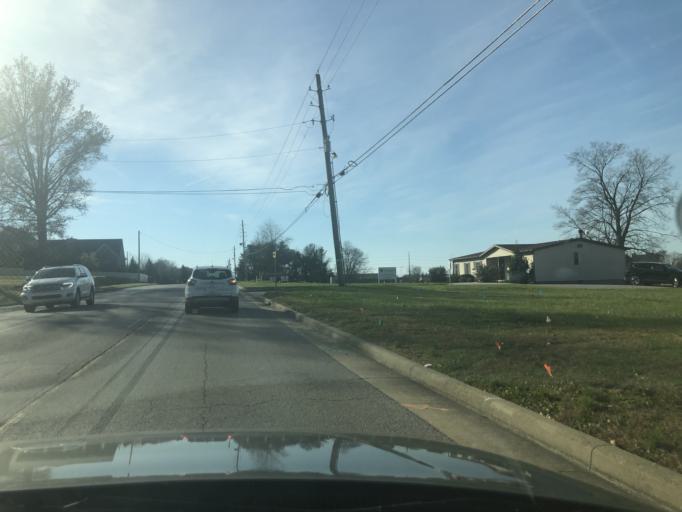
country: US
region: Indiana
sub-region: Warrick County
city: Newburgh
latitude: 37.9727
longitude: -87.4412
